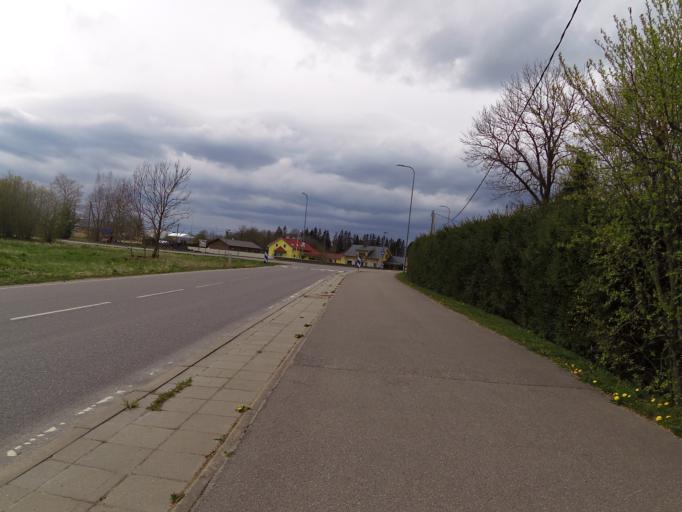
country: EE
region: Harju
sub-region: Rae vald
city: Jueri
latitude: 59.3723
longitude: 24.8367
